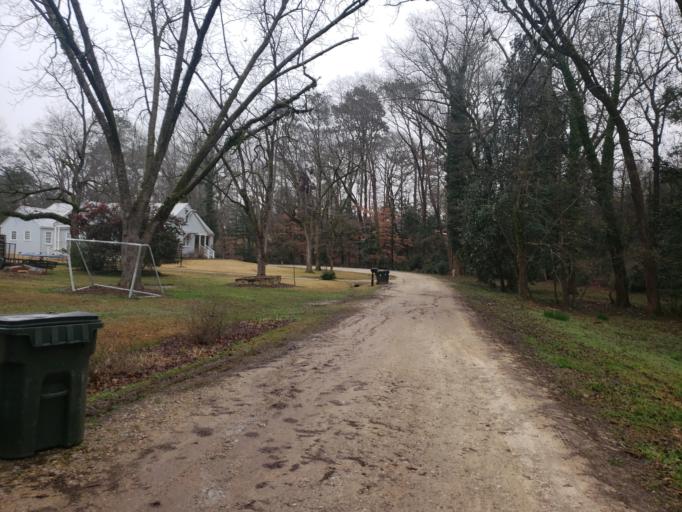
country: US
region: Alabama
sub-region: Lee County
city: Auburn
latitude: 32.5976
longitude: -85.4674
